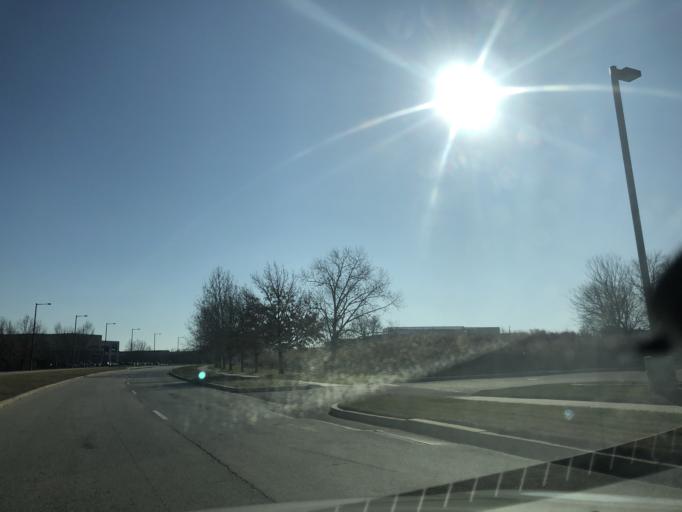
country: US
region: New Jersey
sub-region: Gloucester County
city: National Park
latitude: 39.8960
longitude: -75.1695
